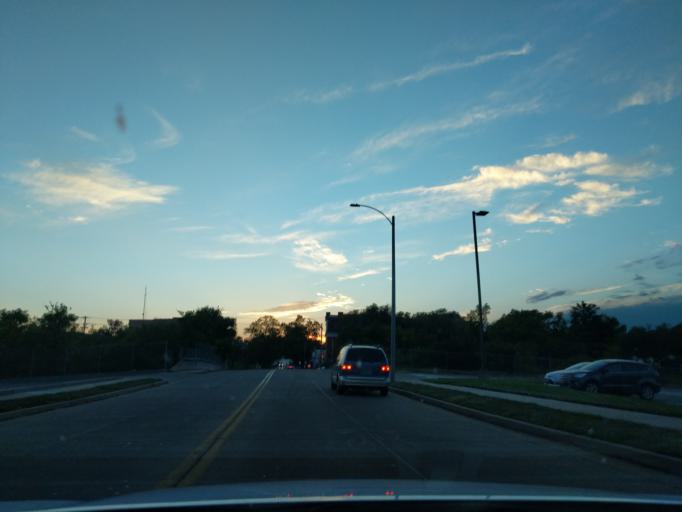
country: US
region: Missouri
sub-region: Saint Louis County
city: Maplewood
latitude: 38.6055
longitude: -90.2743
